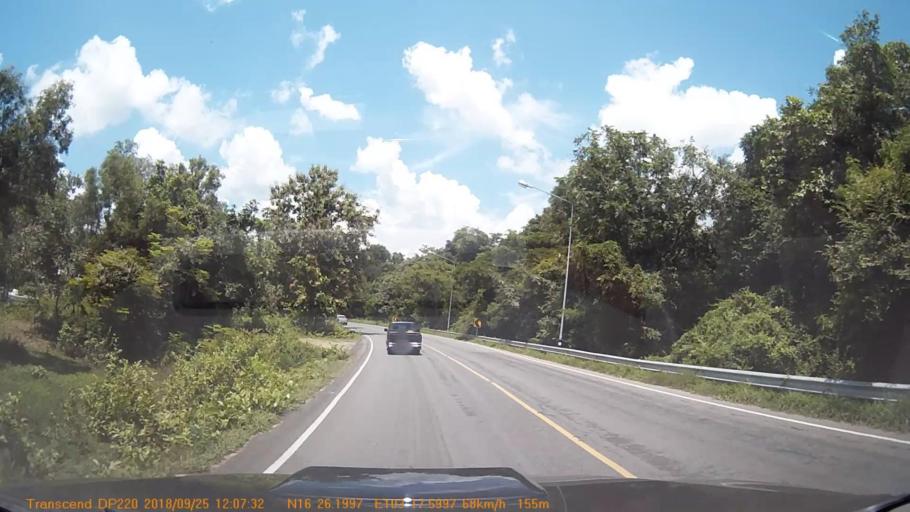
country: TH
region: Kalasin
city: Yang Talat
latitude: 16.4365
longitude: 103.2934
